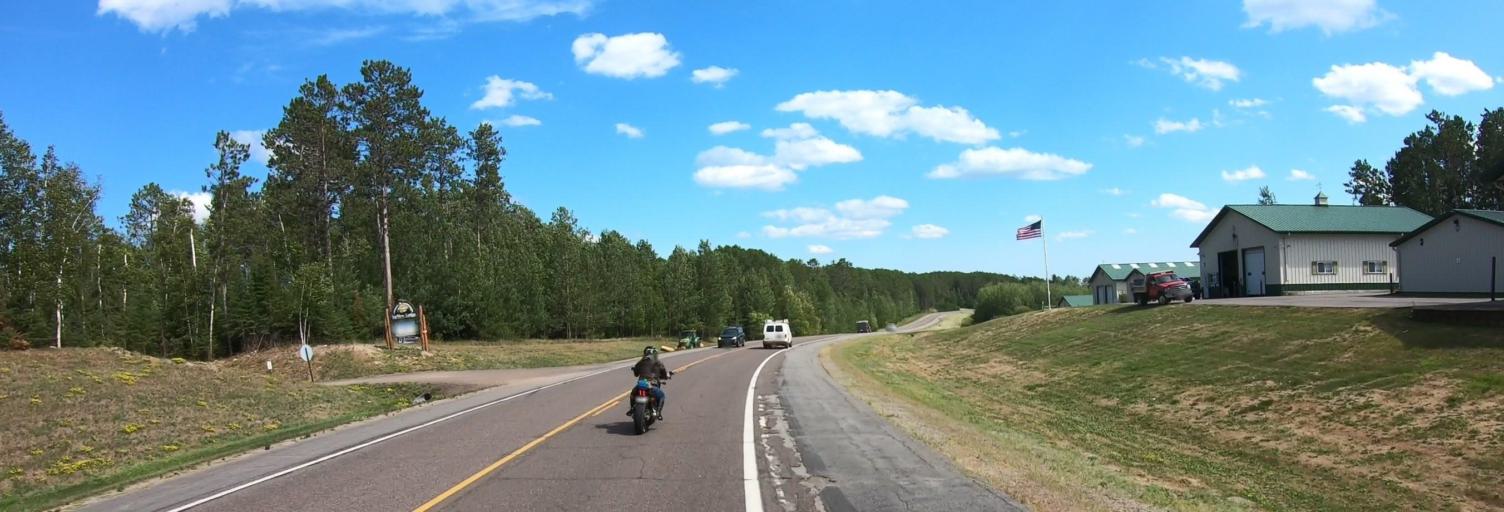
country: US
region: Minnesota
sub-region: Saint Louis County
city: Aurora
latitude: 47.8451
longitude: -92.3805
